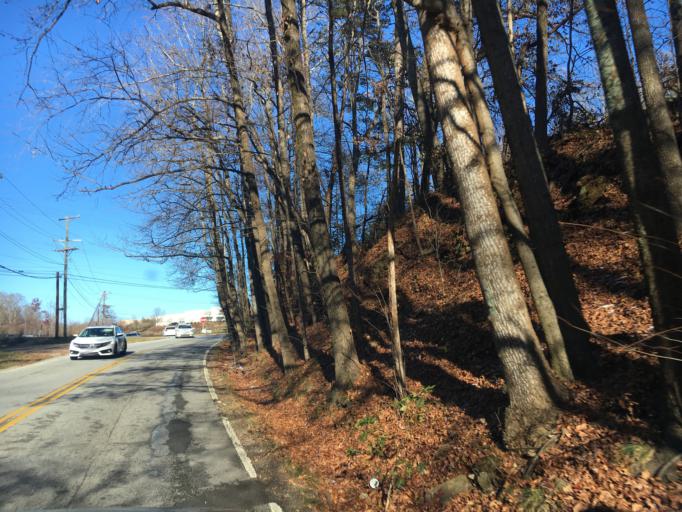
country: US
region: South Carolina
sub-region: Greenville County
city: Taylors
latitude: 34.9328
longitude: -82.2829
